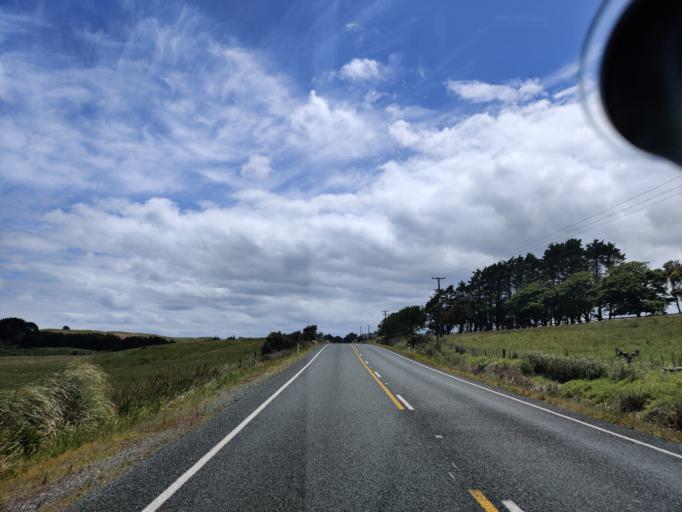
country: NZ
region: Northland
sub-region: Far North District
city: Kaitaia
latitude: -34.7311
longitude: 173.0445
